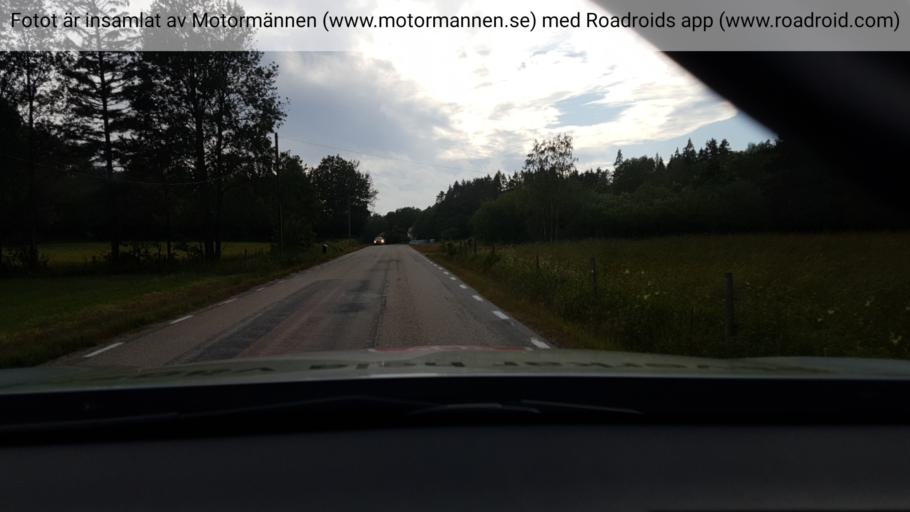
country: SE
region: Vaestra Goetaland
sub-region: Orust
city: Henan
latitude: 58.1586
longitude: 11.6539
